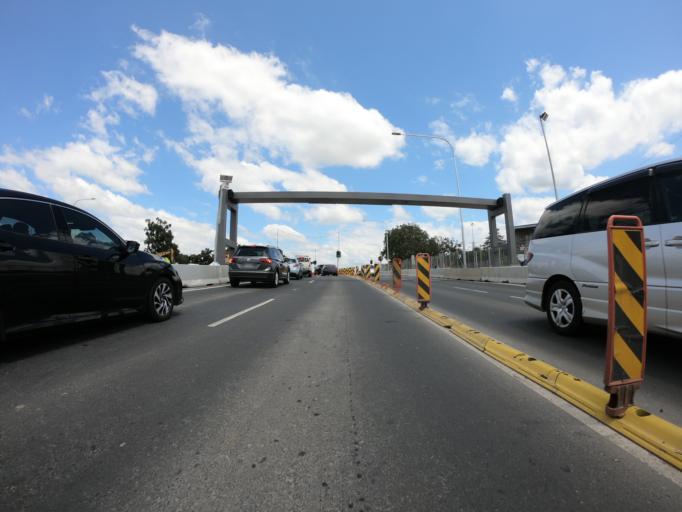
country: AU
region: New South Wales
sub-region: Penrith Municipality
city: Penrith
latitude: -33.7487
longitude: 150.6885
